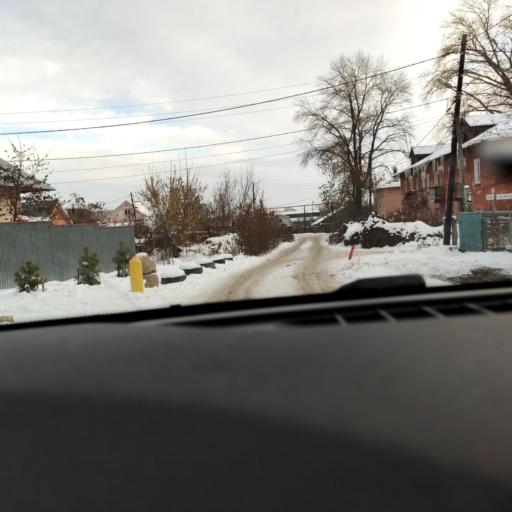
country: RU
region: Samara
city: Samara
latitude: 53.1849
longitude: 50.2105
